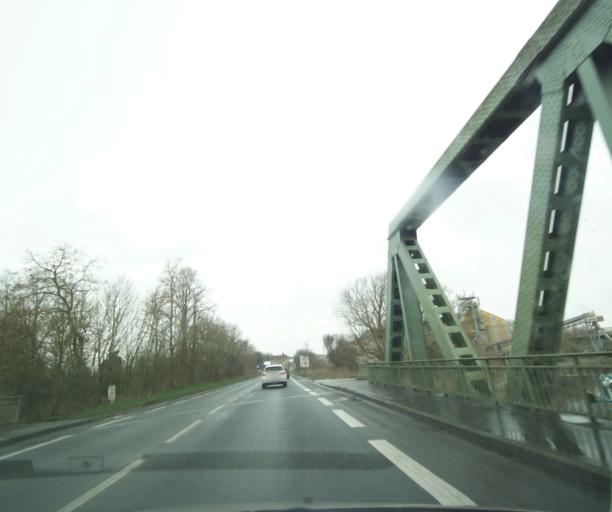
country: FR
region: Nord-Pas-de-Calais
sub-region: Departement du Nord
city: Haulchin
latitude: 50.3230
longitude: 3.4325
